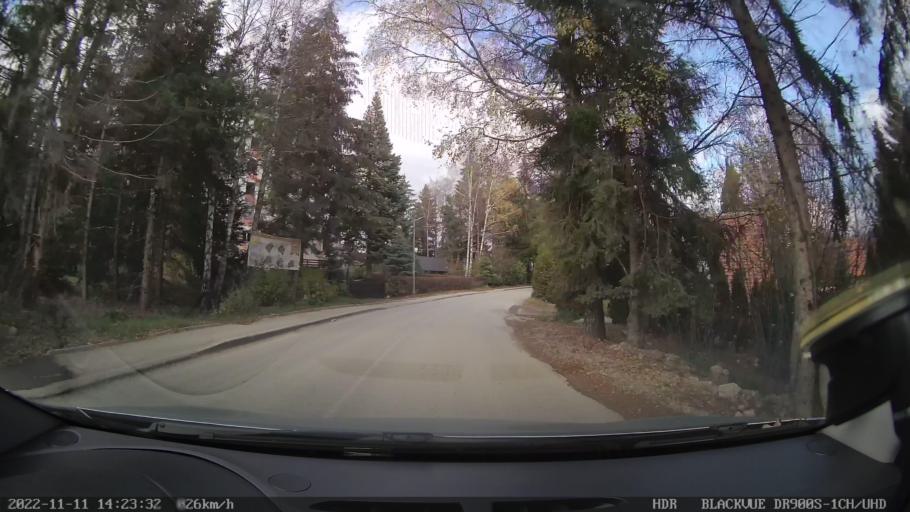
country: RS
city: Zlatibor
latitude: 43.7376
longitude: 19.7002
